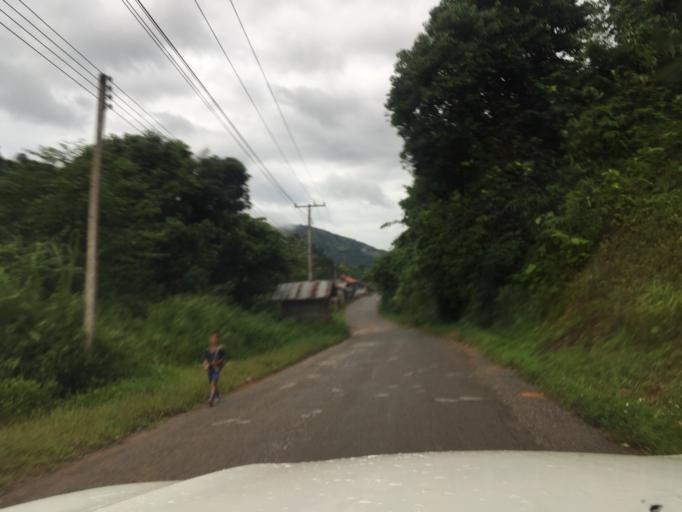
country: LA
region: Oudomxai
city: Muang La
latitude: 20.9828
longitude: 102.2251
